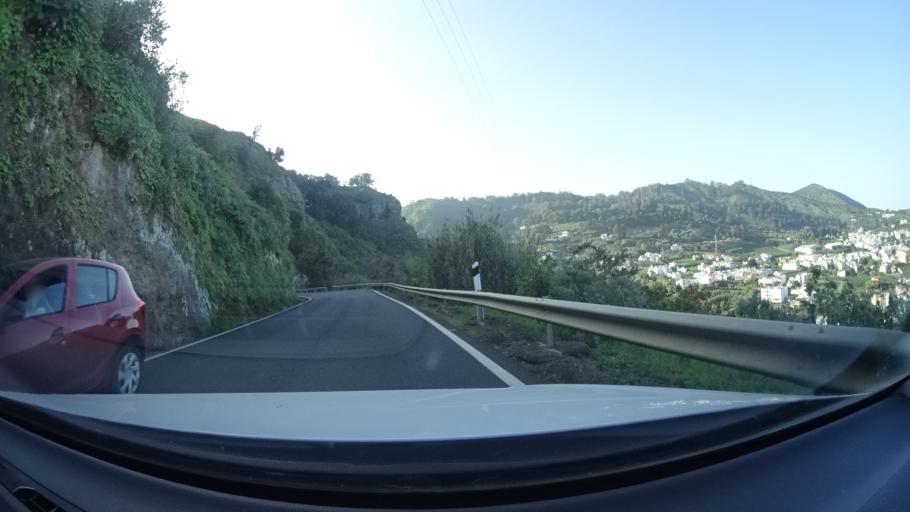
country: ES
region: Canary Islands
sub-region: Provincia de Las Palmas
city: Teror
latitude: 28.0544
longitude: -15.5529
